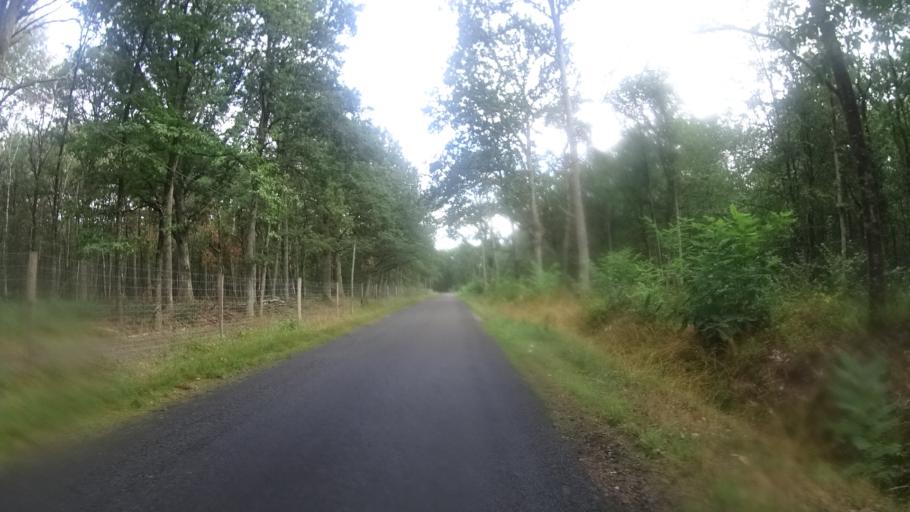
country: FR
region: Centre
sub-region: Departement du Loiret
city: Chateauneuf-sur-Loire
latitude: 47.9037
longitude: 2.2102
